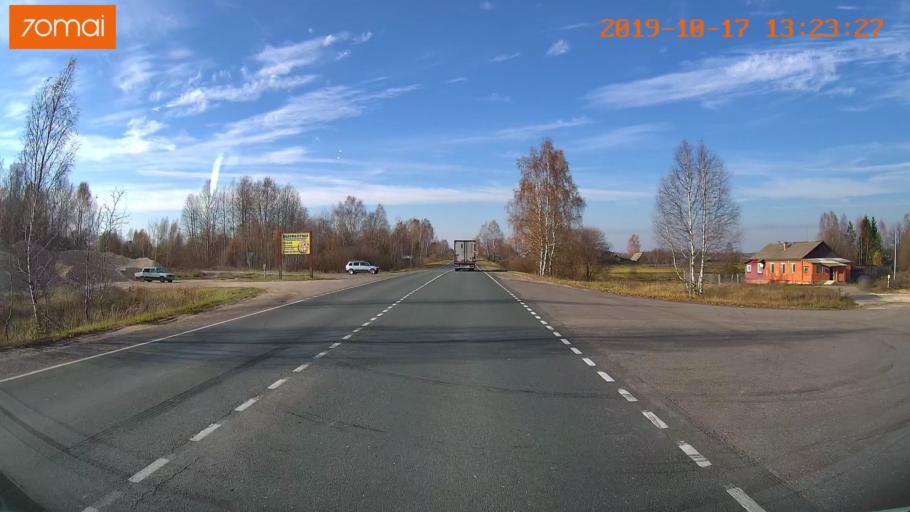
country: RU
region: Rjazan
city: Gus'-Zheleznyy
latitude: 55.0894
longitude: 40.9795
